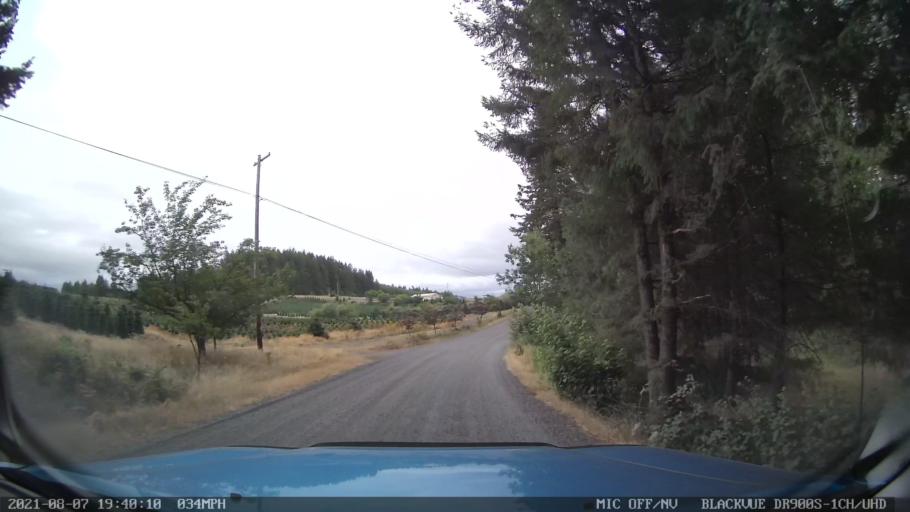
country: US
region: Oregon
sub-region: Marion County
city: Silverton
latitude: 44.9307
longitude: -122.6570
